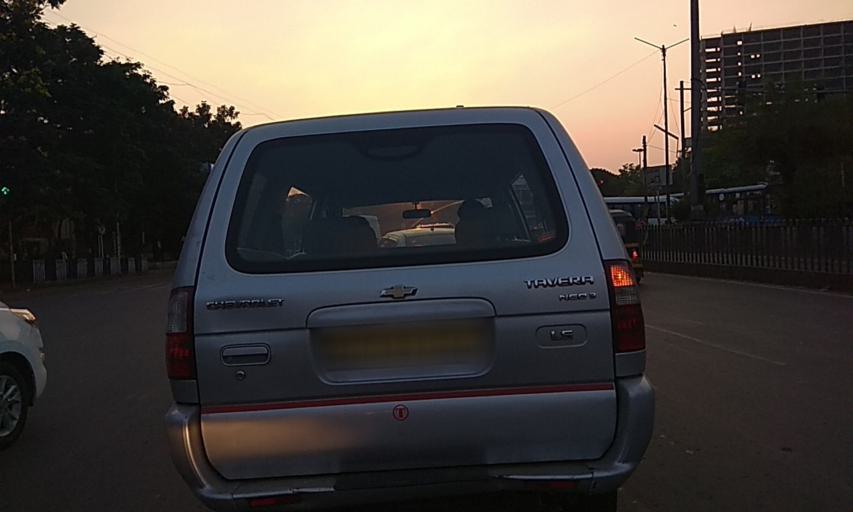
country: IN
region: Maharashtra
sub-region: Pune Division
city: Khadki
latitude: 18.5523
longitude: 73.8970
